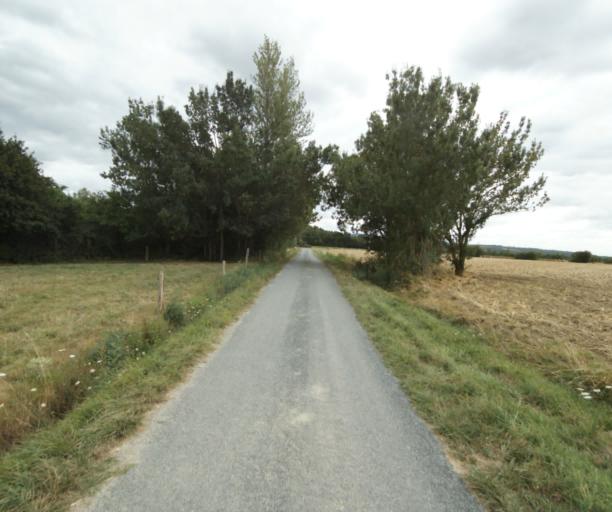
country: FR
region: Midi-Pyrenees
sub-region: Departement du Tarn
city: Soreze
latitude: 43.4735
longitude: 2.0420
